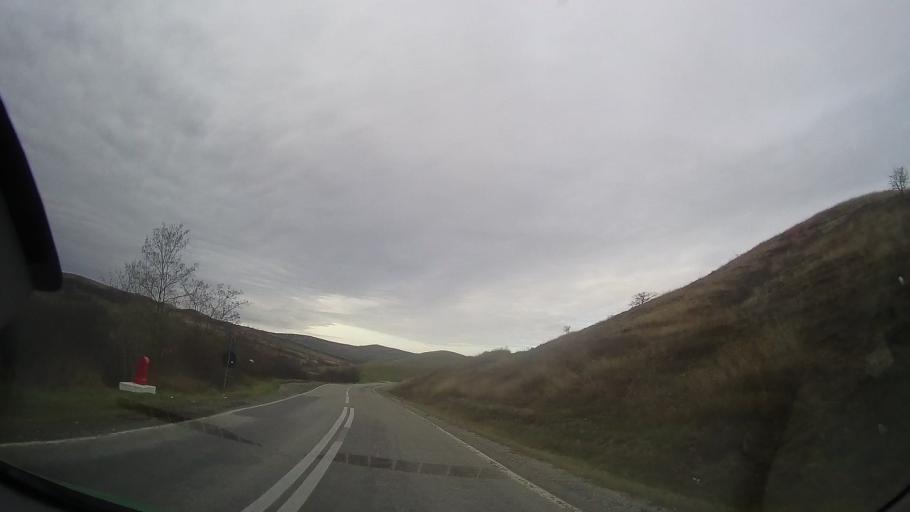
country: RO
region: Mures
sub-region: Comuna Sarmasu
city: Sarmasu
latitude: 46.7948
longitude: 24.1829
